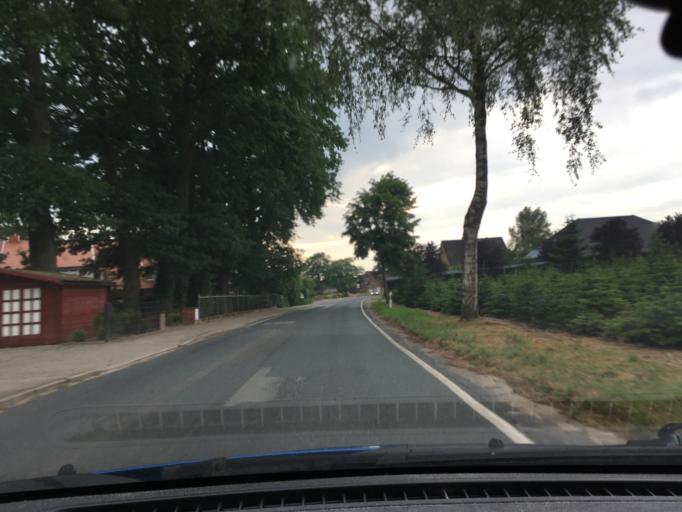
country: DE
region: Lower Saxony
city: Drestedt
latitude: 53.3286
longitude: 9.7712
